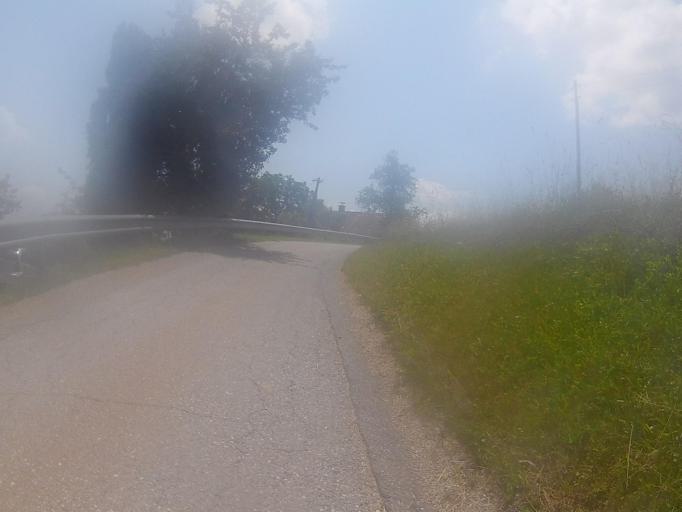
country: SI
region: Maribor
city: Bresternica
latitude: 46.6134
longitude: 15.5638
